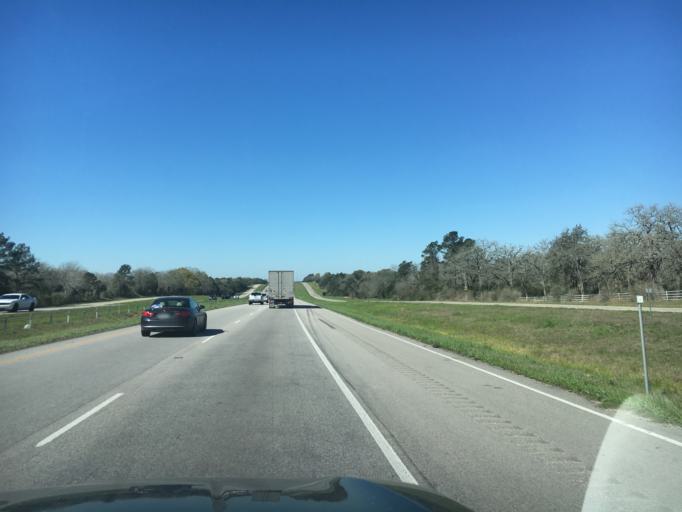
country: US
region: Texas
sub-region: Colorado County
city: Columbus
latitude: 29.7190
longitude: -96.4426
